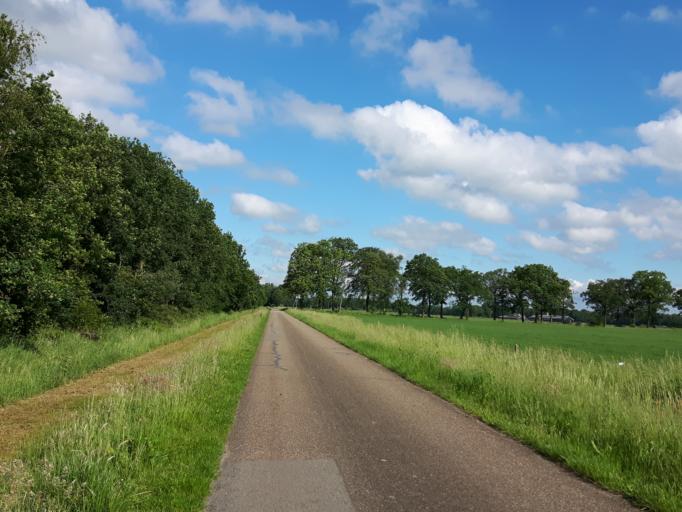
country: NL
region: Overijssel
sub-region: Gemeente Enschede
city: Enschede
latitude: 52.1615
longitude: 6.8402
